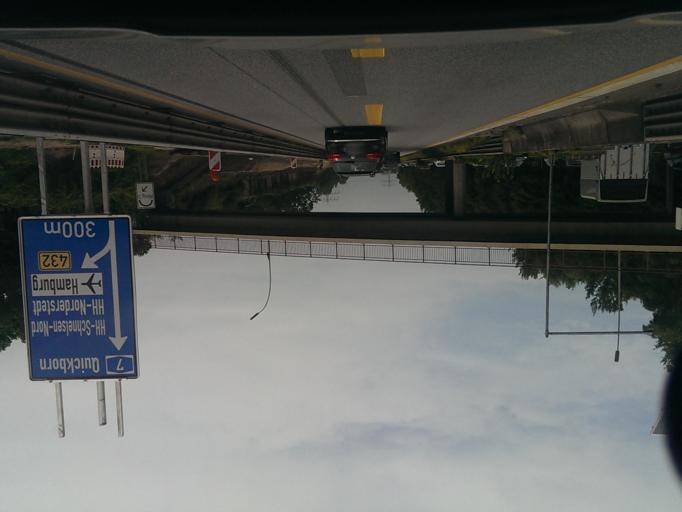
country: DE
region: Schleswig-Holstein
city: Bonningstedt
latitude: 53.6380
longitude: 9.9257
